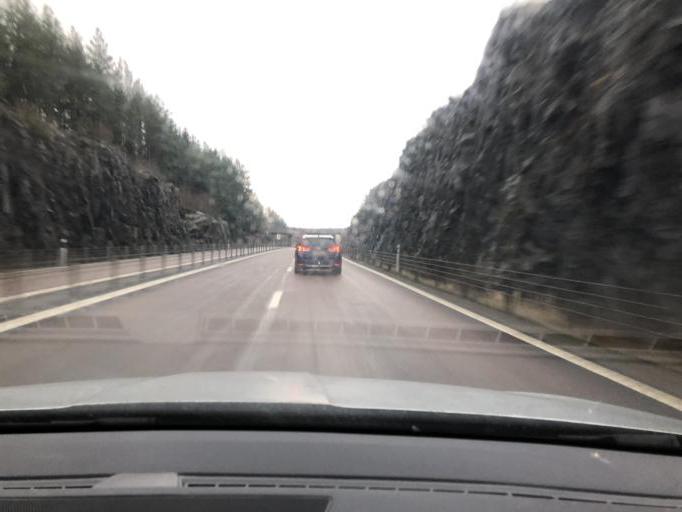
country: SE
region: Vaermland
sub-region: Karlstads Kommun
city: Skattkarr
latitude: 59.4171
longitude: 13.7334
